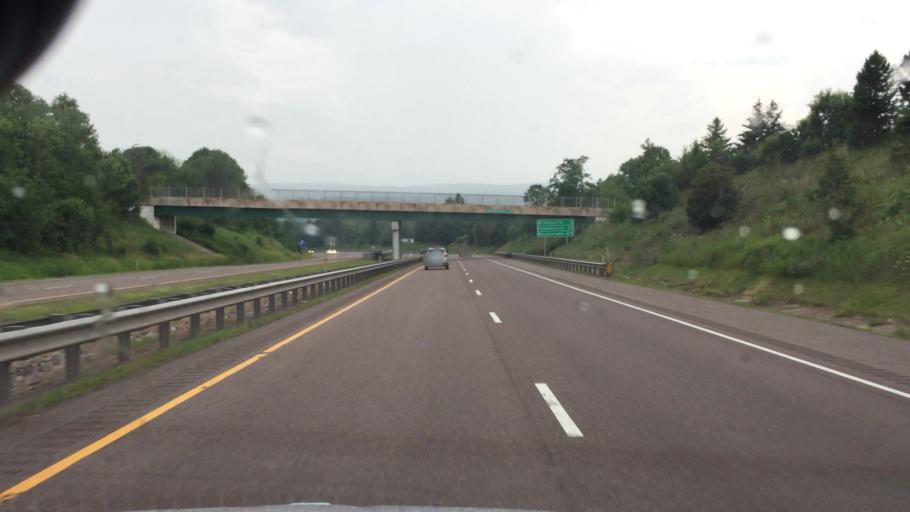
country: US
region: Pennsylvania
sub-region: Somerset County
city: Meyersdale
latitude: 39.6936
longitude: -79.1182
